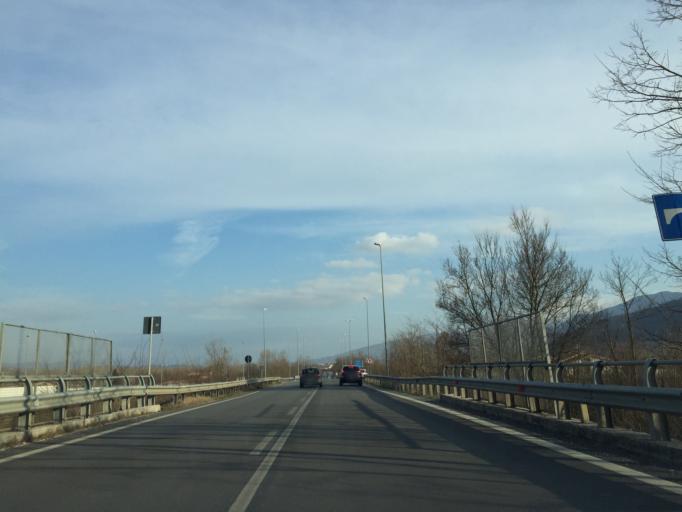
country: IT
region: Molise
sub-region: Provincia di Campobasso
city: Bojano
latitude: 41.4899
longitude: 14.4797
